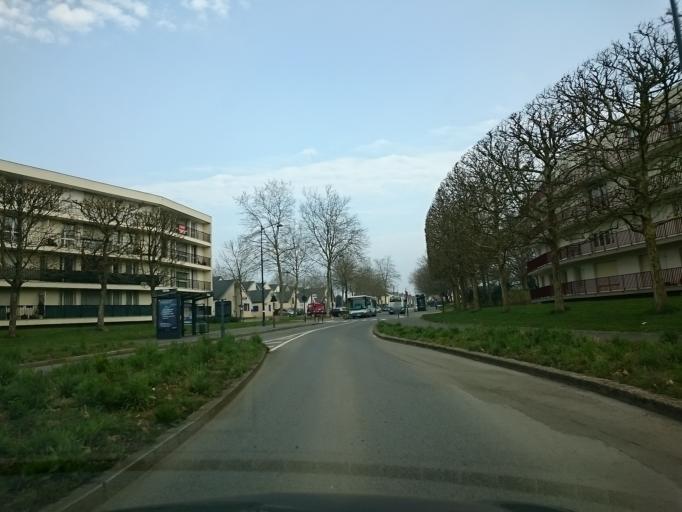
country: FR
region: Brittany
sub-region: Departement d'Ille-et-Vilaine
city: Rennes
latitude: 48.0917
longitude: -1.6583
